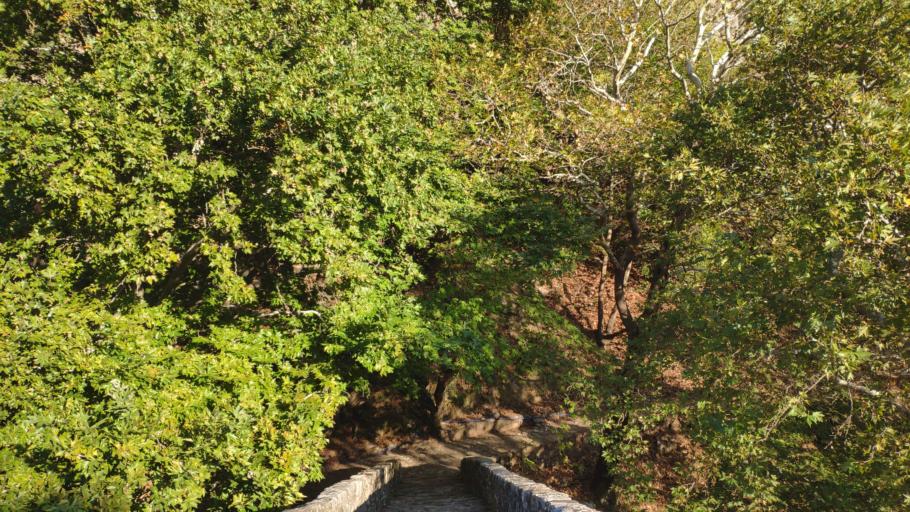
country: GR
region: Thessaly
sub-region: Trikala
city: Pyli
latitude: 39.4605
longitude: 21.6004
